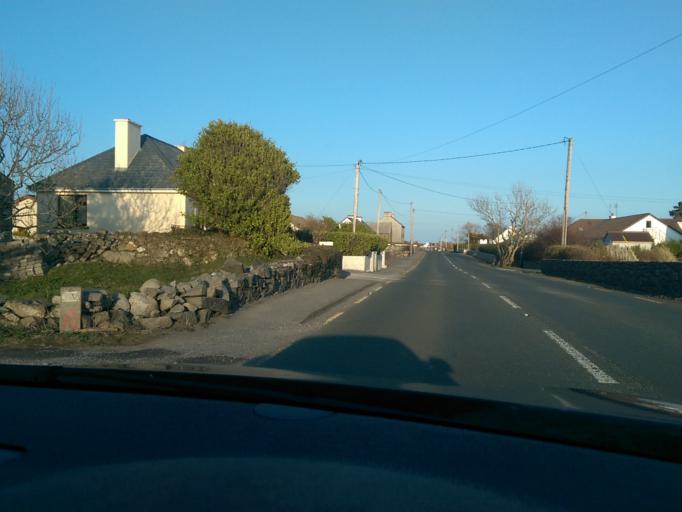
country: IE
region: Connaught
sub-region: County Galway
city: Oughterard
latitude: 53.2441
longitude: -9.3389
